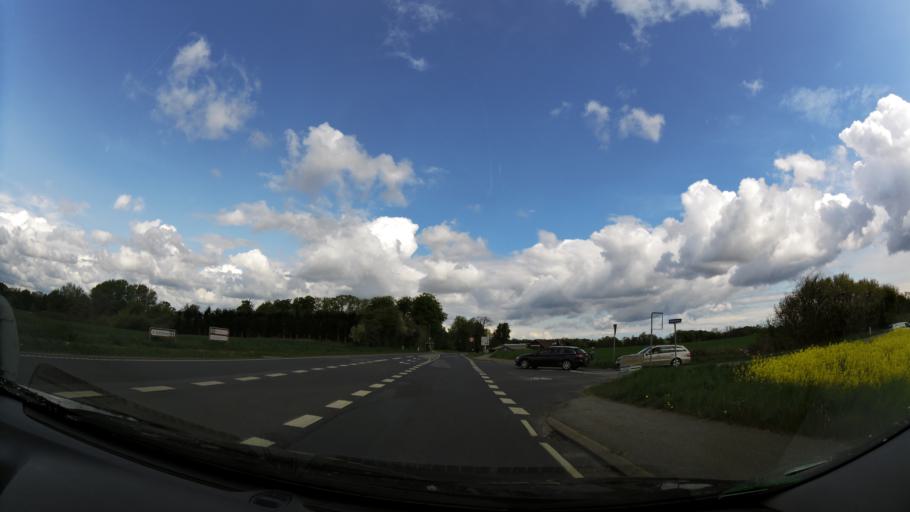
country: DK
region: South Denmark
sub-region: Svendborg Kommune
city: Thuro By
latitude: 55.1346
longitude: 10.7313
